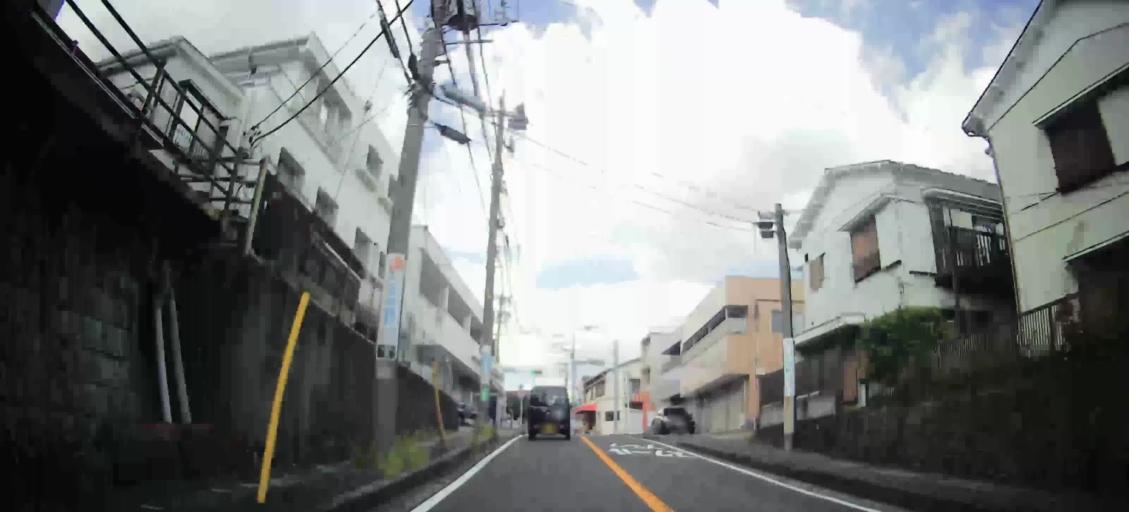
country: JP
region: Kanagawa
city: Yokohama
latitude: 35.4624
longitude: 139.5607
